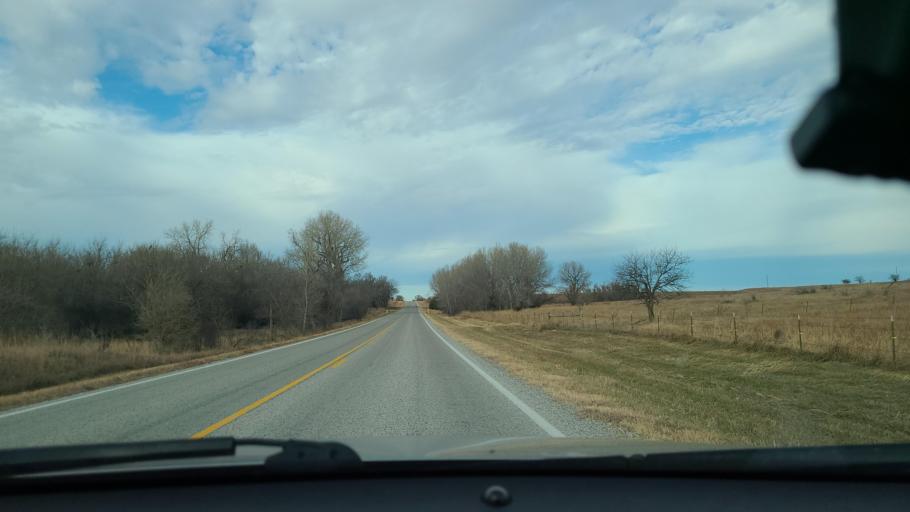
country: US
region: Kansas
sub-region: McPherson County
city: Inman
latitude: 38.3448
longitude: -97.9246
